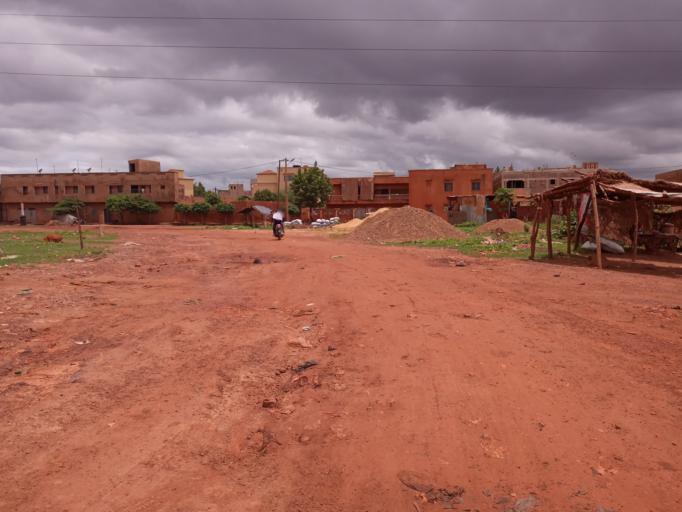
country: ML
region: Bamako
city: Bamako
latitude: 12.5479
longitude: -7.9953
